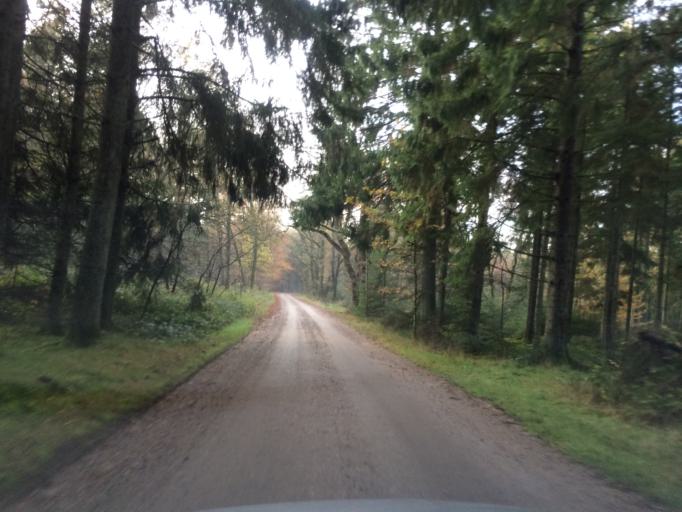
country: DK
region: Central Jutland
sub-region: Holstebro Kommune
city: Ulfborg
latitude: 56.2567
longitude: 8.3628
